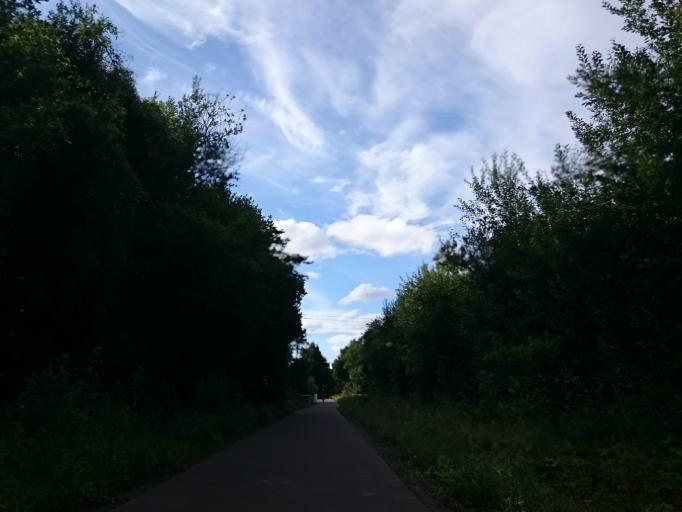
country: FR
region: Lower Normandy
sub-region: Departement du Calvados
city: Saint-Andre-sur-Orne
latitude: 49.1244
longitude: -0.4006
